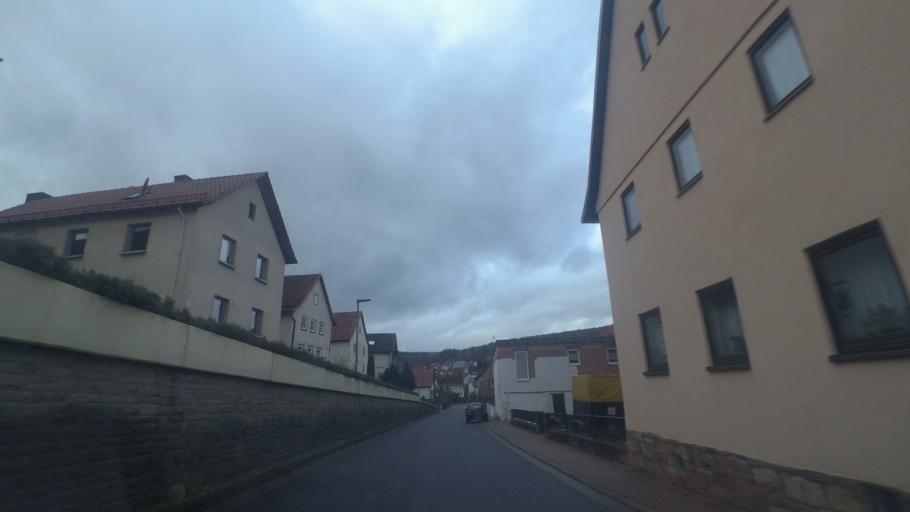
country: DE
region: Bavaria
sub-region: Regierungsbezirk Unterfranken
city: Hohenroth
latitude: 50.3564
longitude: 10.1104
